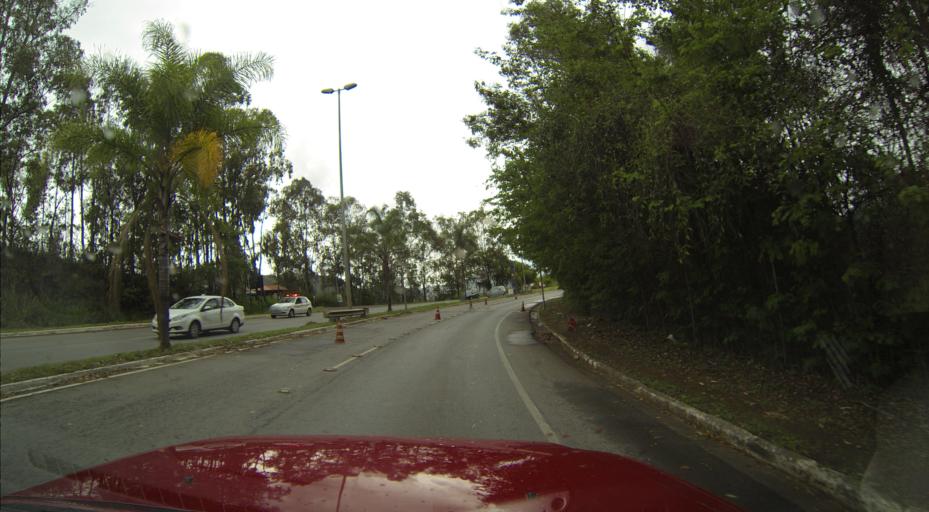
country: BR
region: Minas Gerais
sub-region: Nova Lima
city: Nova Lima
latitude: -20.0015
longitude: -43.9022
